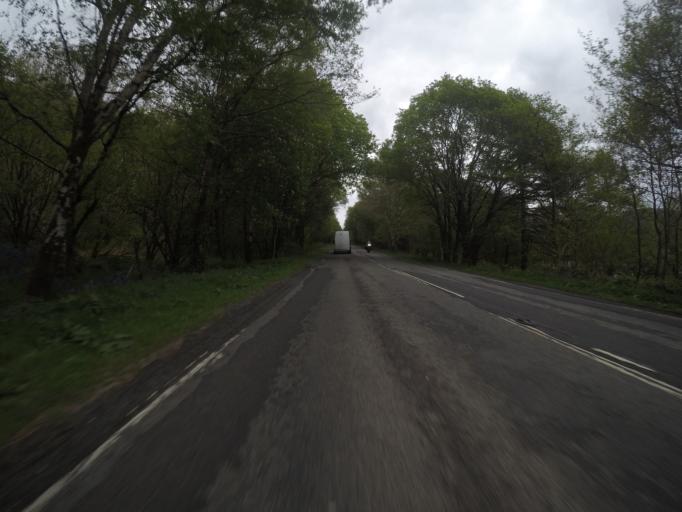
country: GB
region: Scotland
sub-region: Highland
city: Fort William
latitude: 57.2501
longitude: -5.4720
